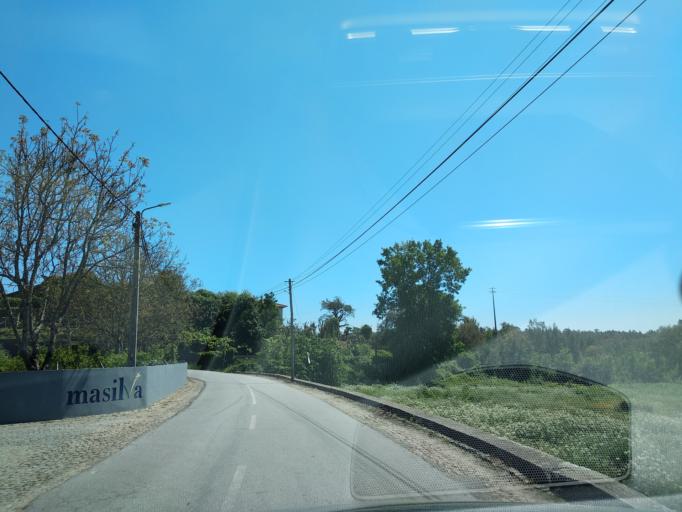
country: PT
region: Porto
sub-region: Paredes
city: Gandra
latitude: 41.1855
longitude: -8.4260
